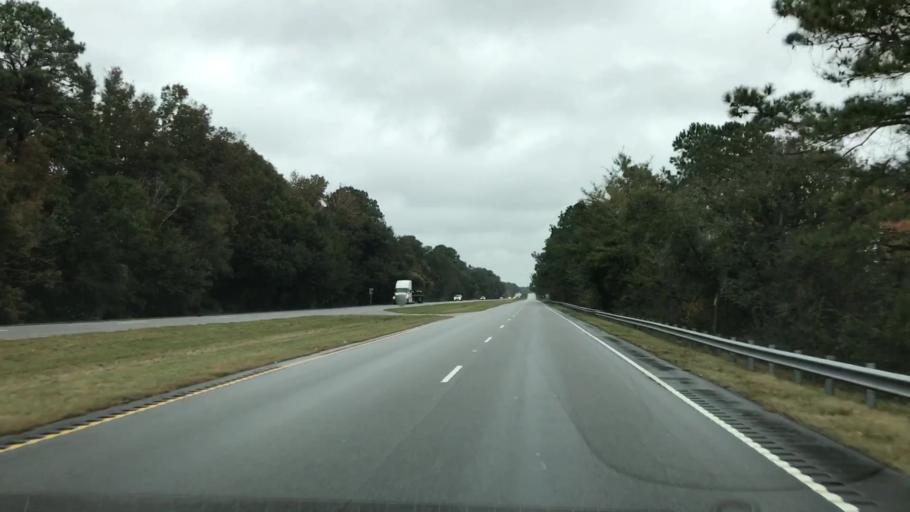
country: US
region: South Carolina
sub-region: Georgetown County
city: Georgetown
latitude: 33.1994
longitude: -79.3925
